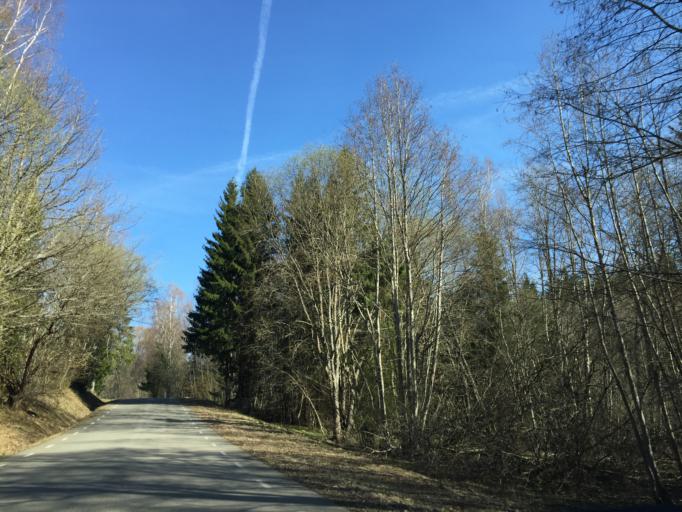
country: EE
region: Vorumaa
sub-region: Antsla vald
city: Vana-Antsla
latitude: 58.0174
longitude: 26.4570
